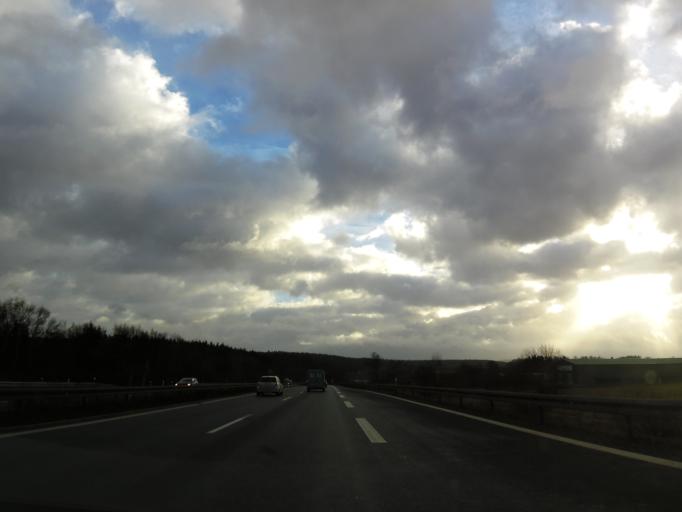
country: DE
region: Bavaria
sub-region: Upper Franconia
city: Selb
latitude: 50.1671
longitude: 12.1073
